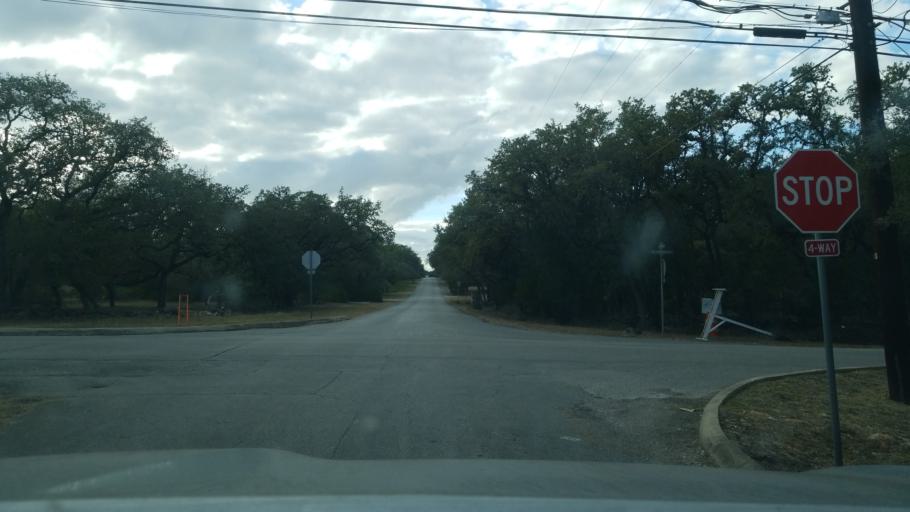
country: US
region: Texas
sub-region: Bexar County
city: Hollywood Park
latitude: 29.5984
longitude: -98.4820
